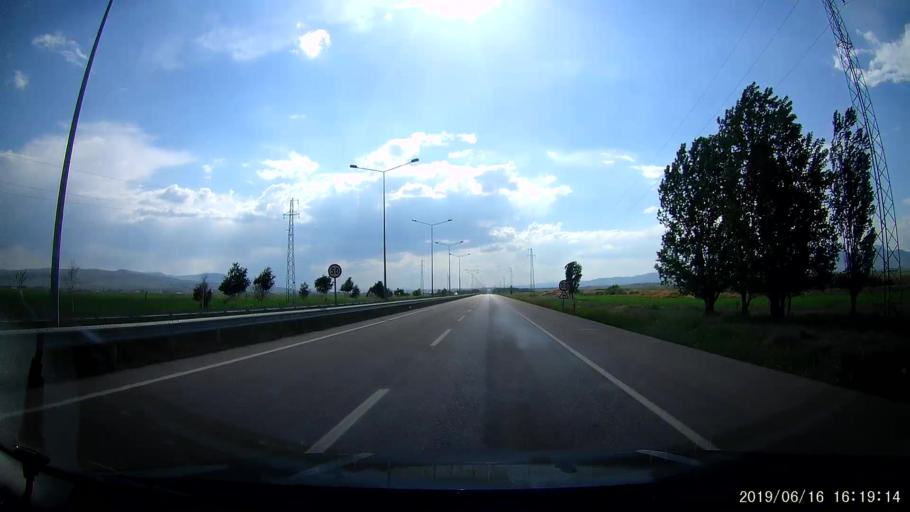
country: TR
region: Erzurum
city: Ilica
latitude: 39.9659
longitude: 41.1470
